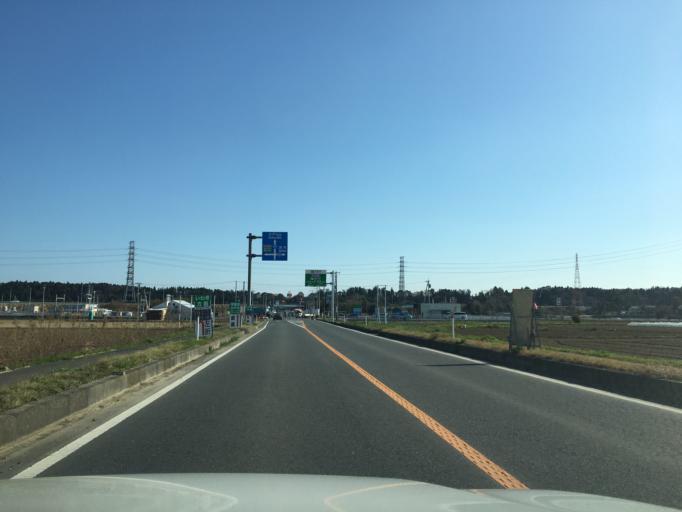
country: JP
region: Ibaraki
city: Mito-shi
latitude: 36.4204
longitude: 140.4234
